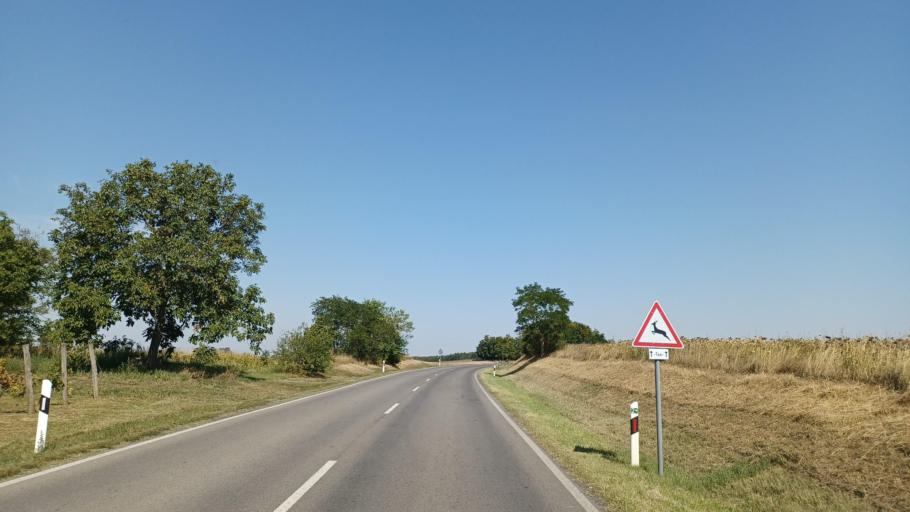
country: HU
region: Tolna
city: Nagydorog
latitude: 46.6447
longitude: 18.6491
